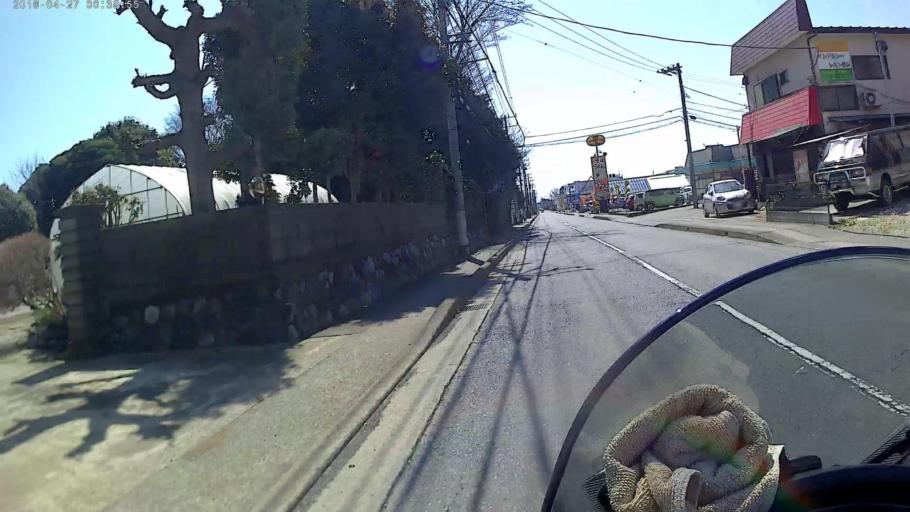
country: JP
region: Kanagawa
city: Atsugi
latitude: 35.4020
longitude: 139.4115
